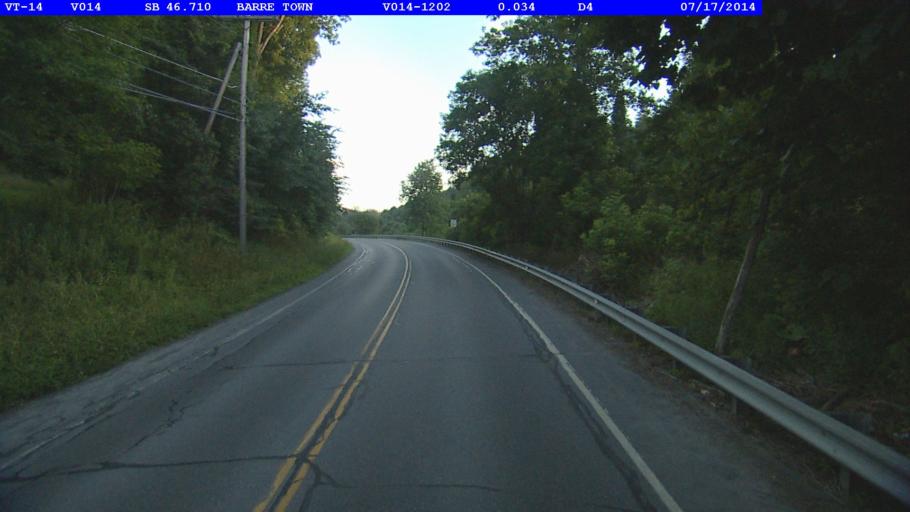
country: US
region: Vermont
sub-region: Washington County
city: South Barre
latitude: 44.1523
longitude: -72.5210
